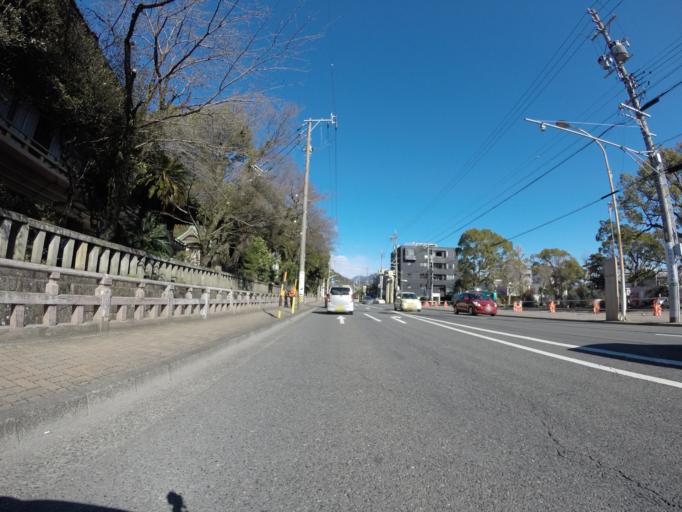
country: JP
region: Shizuoka
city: Shizuoka-shi
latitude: 34.9833
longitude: 138.3764
